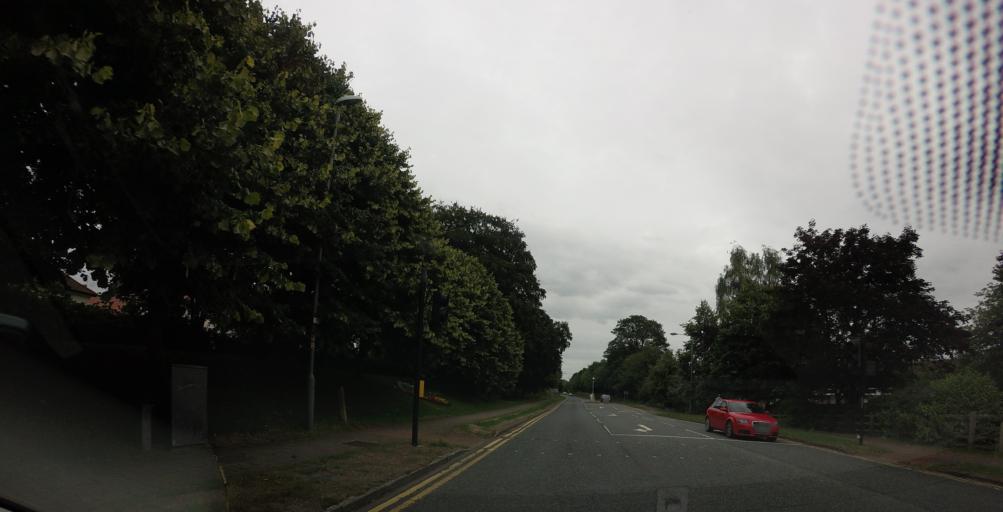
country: GB
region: England
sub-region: North Yorkshire
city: Ripon
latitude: 54.1389
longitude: -1.5176
